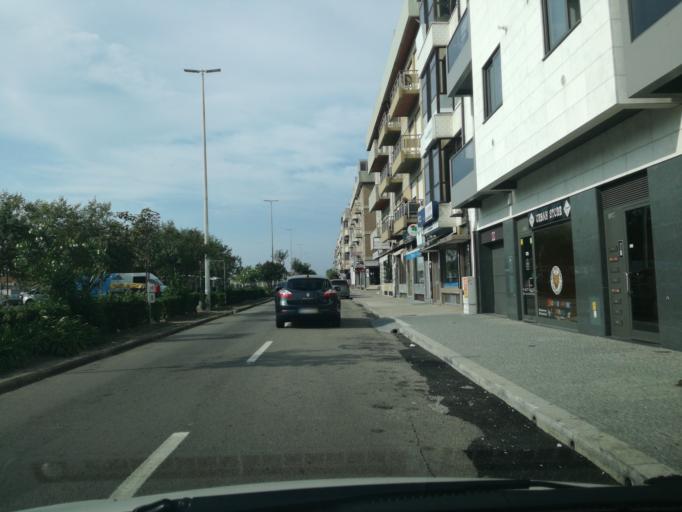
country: PT
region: Aveiro
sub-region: Espinho
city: Espinho
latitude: 41.0042
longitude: -8.6381
